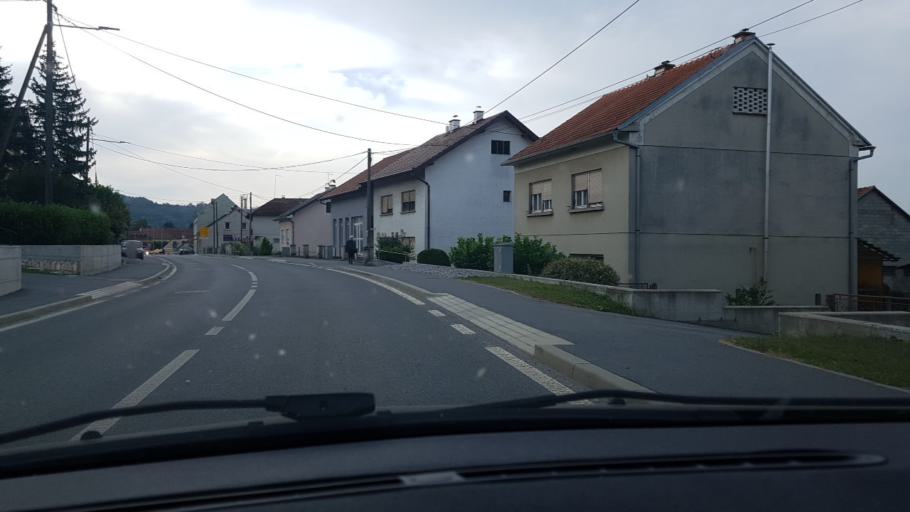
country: HR
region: Krapinsko-Zagorska
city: Zlatar
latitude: 46.0943
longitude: 16.0746
